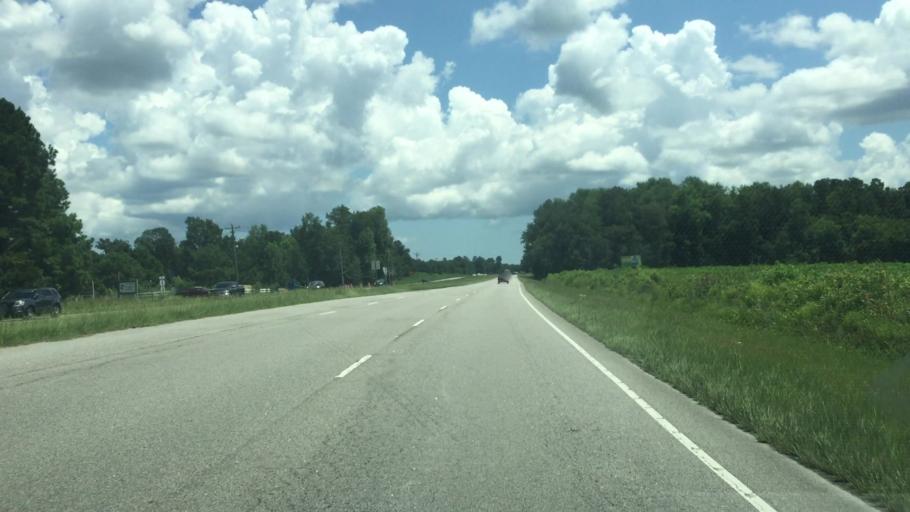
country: US
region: South Carolina
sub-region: Horry County
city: Loris
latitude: 34.0063
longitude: -78.7623
